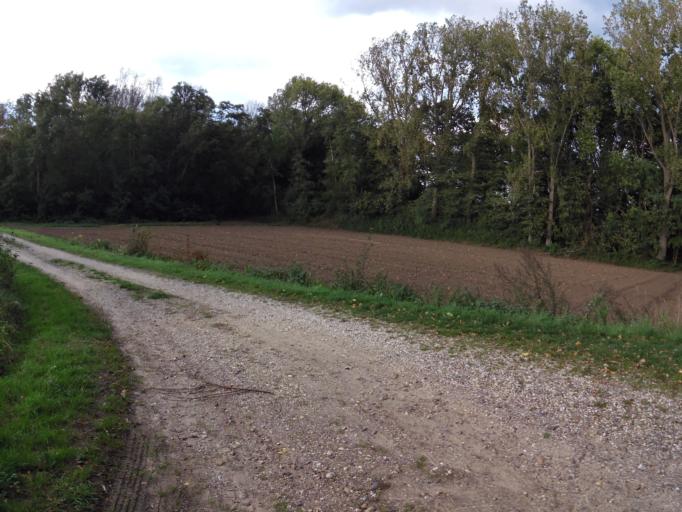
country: NL
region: Limburg
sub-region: Gemeente Maasgouw
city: Maasbracht
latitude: 51.1522
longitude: 5.9216
